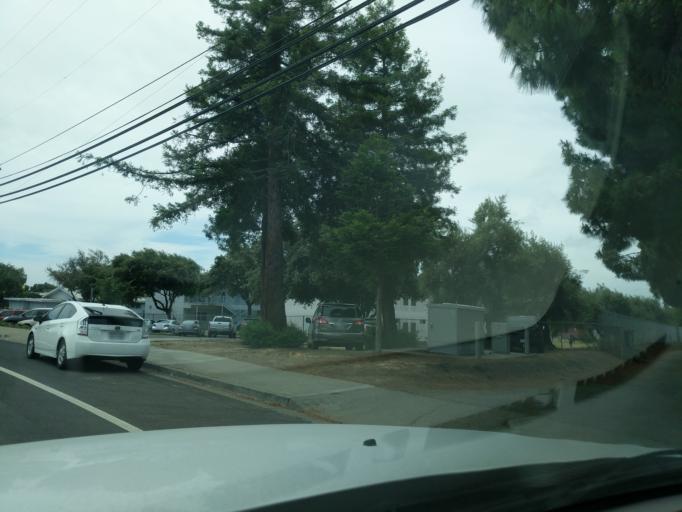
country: US
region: California
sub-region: Alameda County
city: Hayward
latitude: 37.6442
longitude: -122.0669
